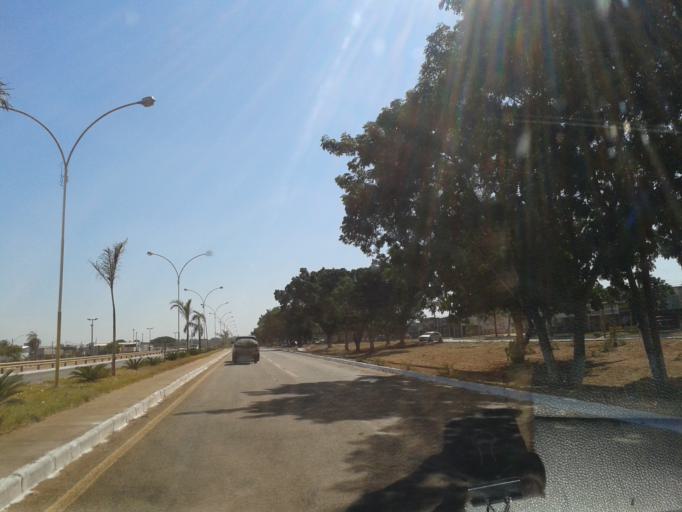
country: BR
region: Goias
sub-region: Crixas
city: Crixas
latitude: -14.0976
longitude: -50.3378
